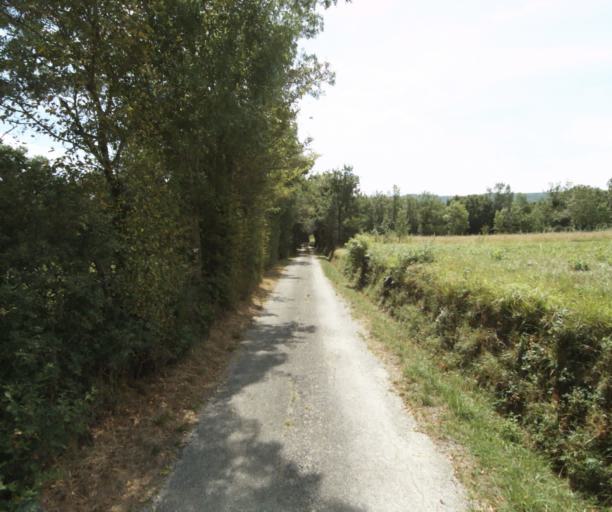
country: FR
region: Midi-Pyrenees
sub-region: Departement du Tarn
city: Soreze
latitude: 43.4756
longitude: 2.0763
